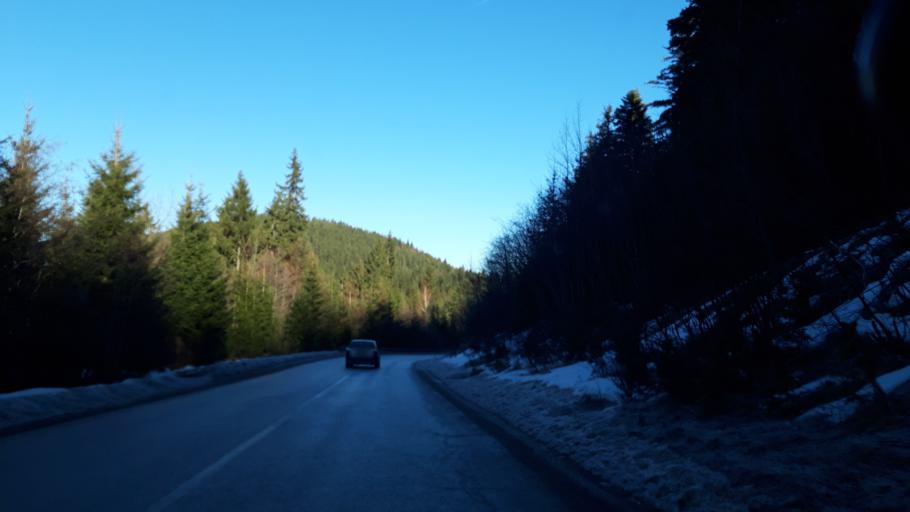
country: BA
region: Republika Srpska
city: Koran
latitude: 43.7848
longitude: 18.5533
